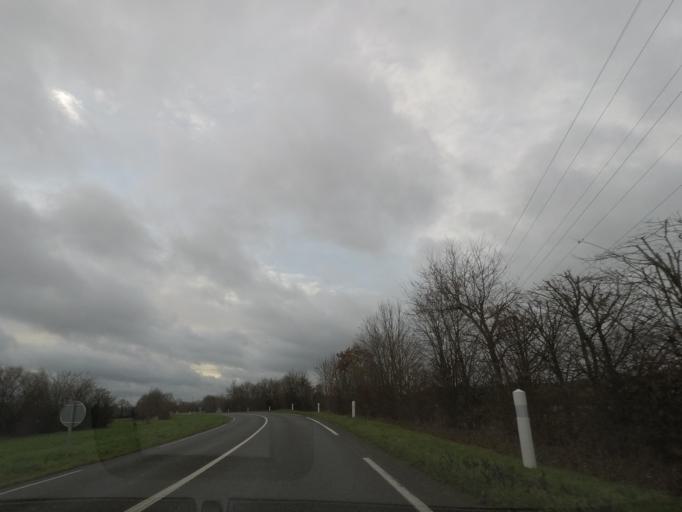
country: FR
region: Pays de la Loire
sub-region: Departement de la Sarthe
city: La Ferte-Bernard
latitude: 48.1902
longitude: 0.6267
